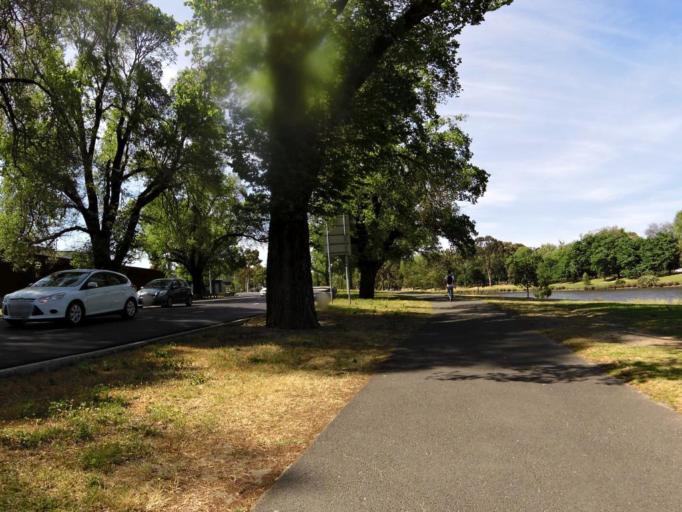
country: AU
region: Victoria
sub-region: Melbourne
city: East Melbourne
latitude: -37.8253
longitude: 144.9800
